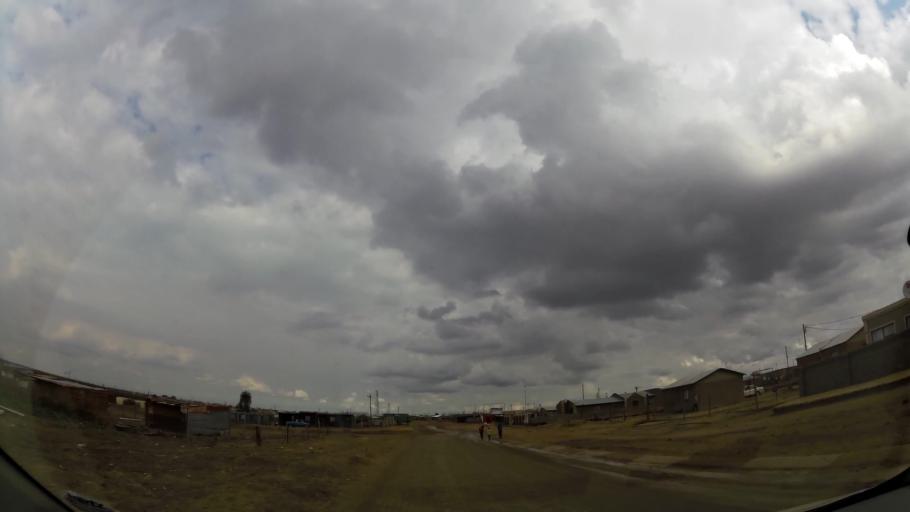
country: ZA
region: Orange Free State
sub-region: Fezile Dabi District Municipality
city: Sasolburg
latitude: -26.8745
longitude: 27.8732
